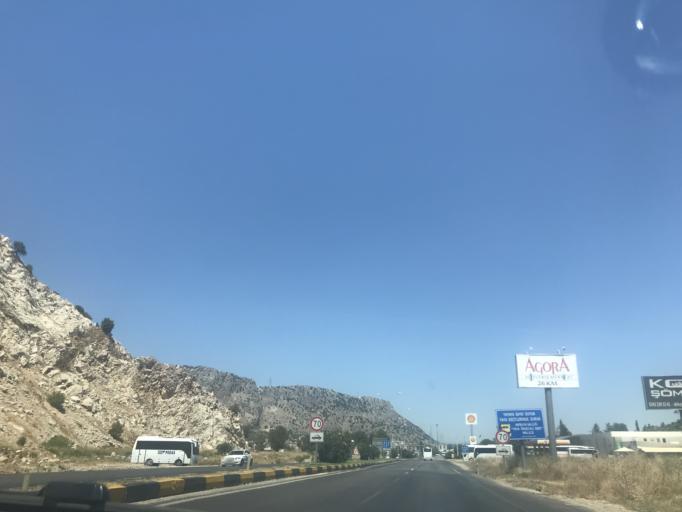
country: TR
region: Antalya
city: Cakirlar
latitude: 36.8315
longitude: 30.5954
